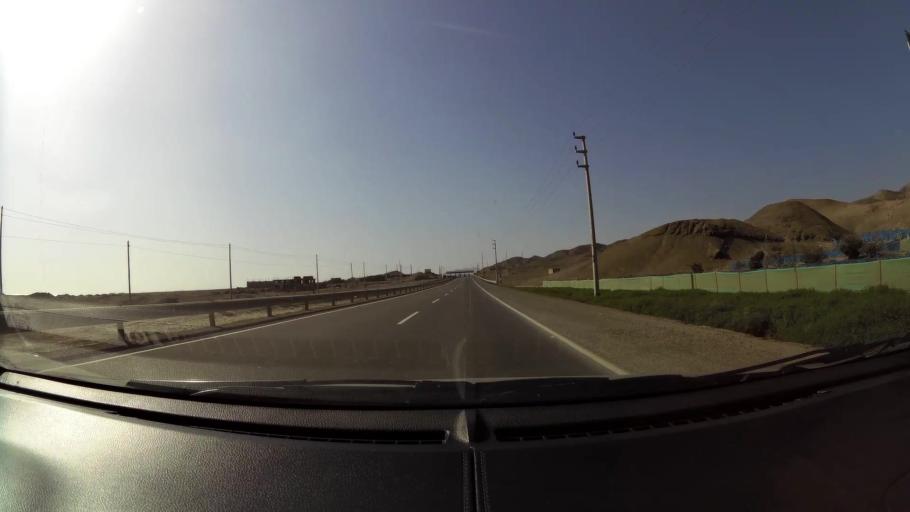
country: PE
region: Ancash
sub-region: Provincia de Huarmey
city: La Caleta Culebras
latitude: -9.9291
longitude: -78.2199
